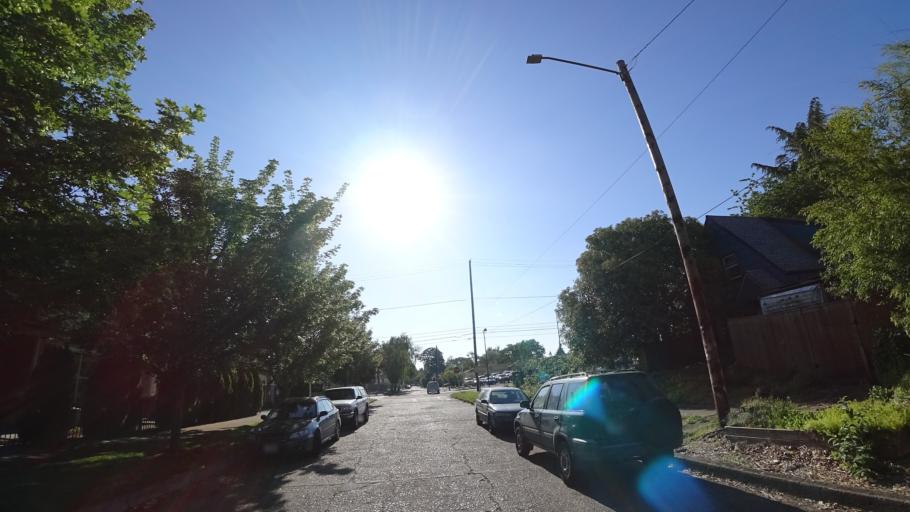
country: US
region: Oregon
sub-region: Multnomah County
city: Portland
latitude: 45.5733
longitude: -122.6621
